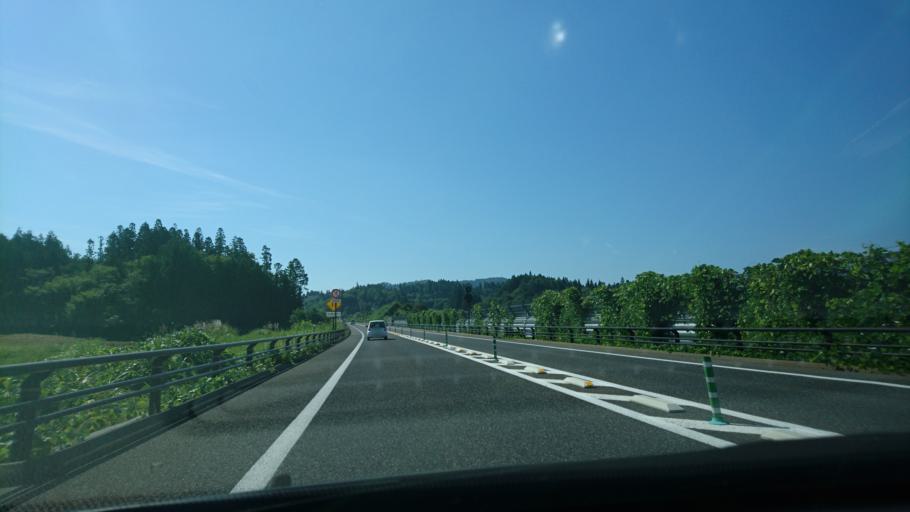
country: JP
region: Iwate
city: Hanamaki
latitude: 39.3477
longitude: 141.2415
